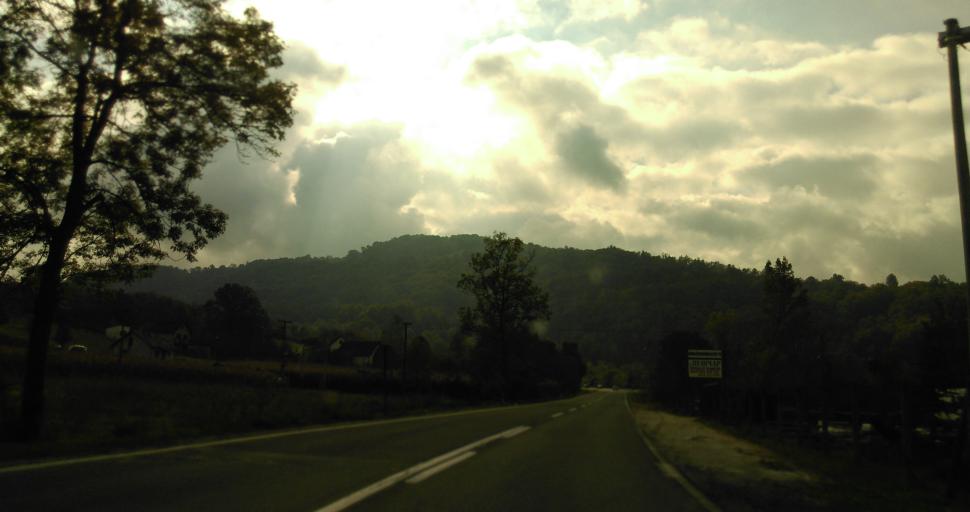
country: RS
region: Central Serbia
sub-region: Kolubarski Okrug
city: Ljig
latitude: 44.2029
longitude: 20.2331
